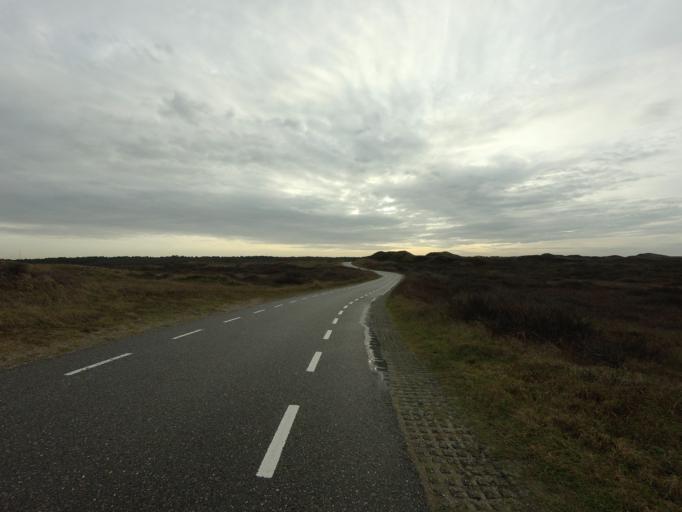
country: NL
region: North Holland
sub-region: Gemeente Texel
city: Den Burg
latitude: 53.0622
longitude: 4.7267
